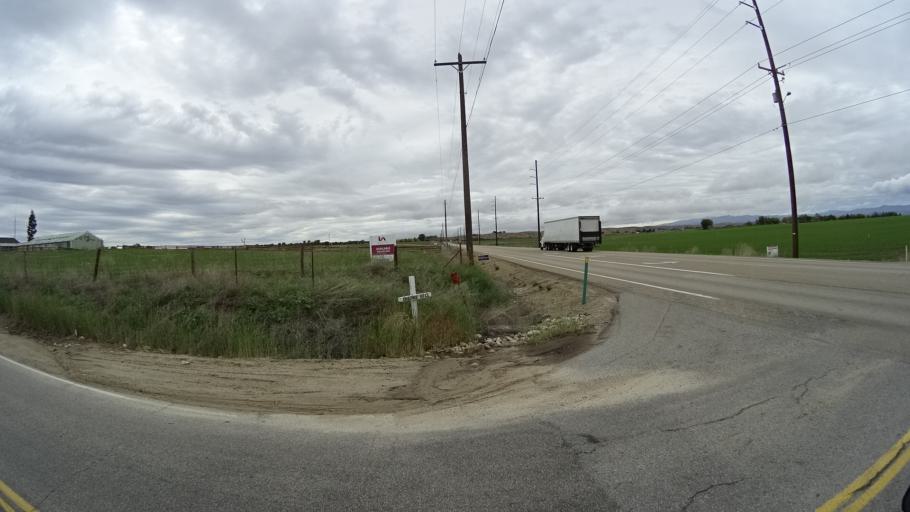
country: US
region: Idaho
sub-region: Ada County
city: Star
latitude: 43.7100
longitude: -116.4586
